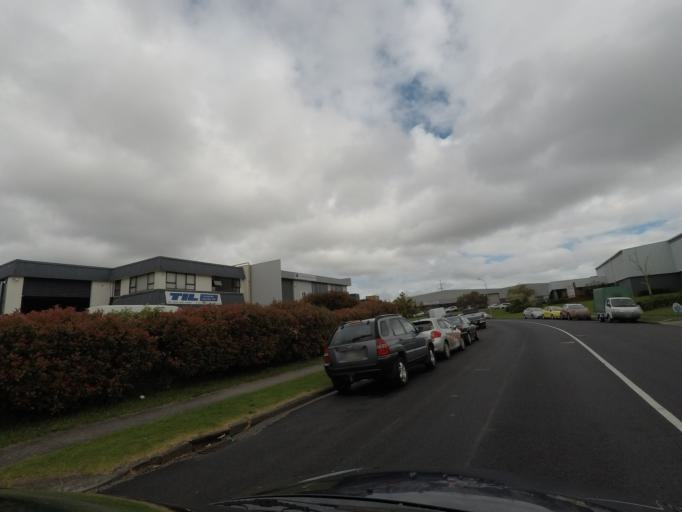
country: NZ
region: Auckland
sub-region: Auckland
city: Tamaki
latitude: -36.9330
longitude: 174.8839
